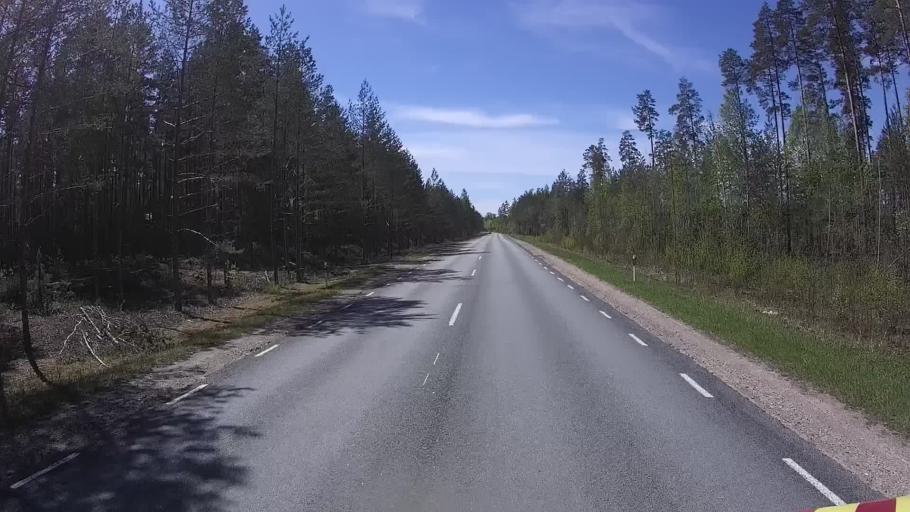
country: EE
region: Polvamaa
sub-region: Polva linn
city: Polva
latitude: 57.9708
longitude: 27.2766
